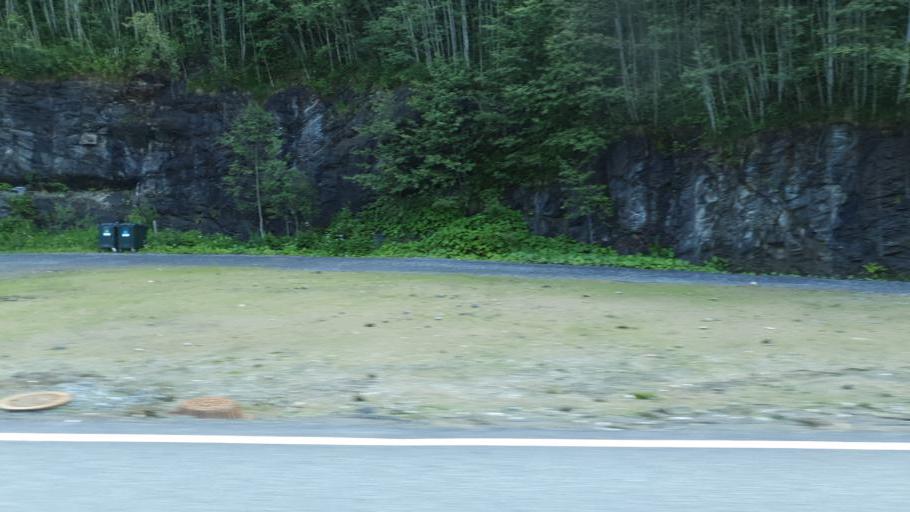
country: NO
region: Sor-Trondelag
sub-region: Midtre Gauldal
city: Storen
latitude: 62.9820
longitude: 10.2357
